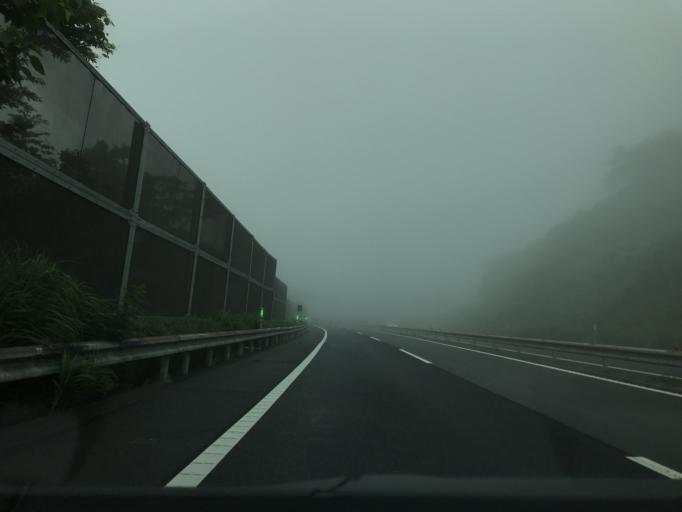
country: JP
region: Oita
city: Hiji
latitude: 33.3659
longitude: 131.4538
